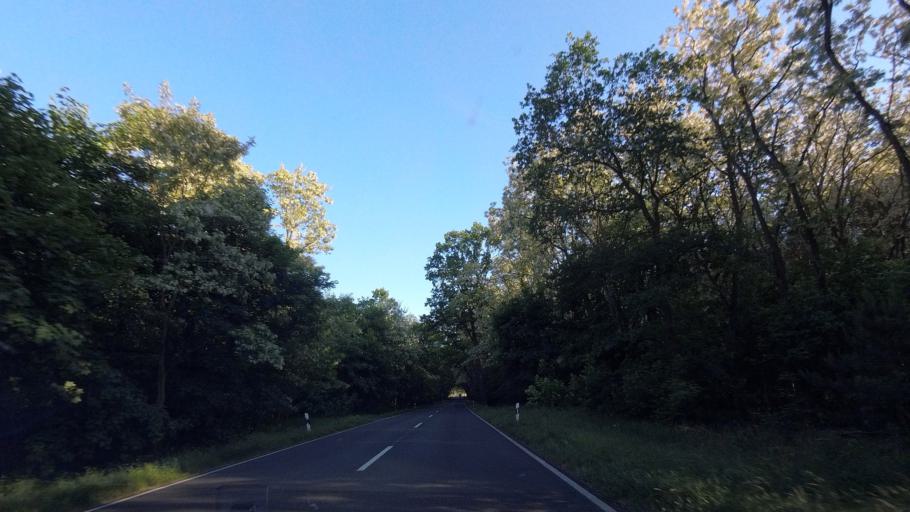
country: DE
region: Brandenburg
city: Golzow
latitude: 52.3194
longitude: 12.6076
